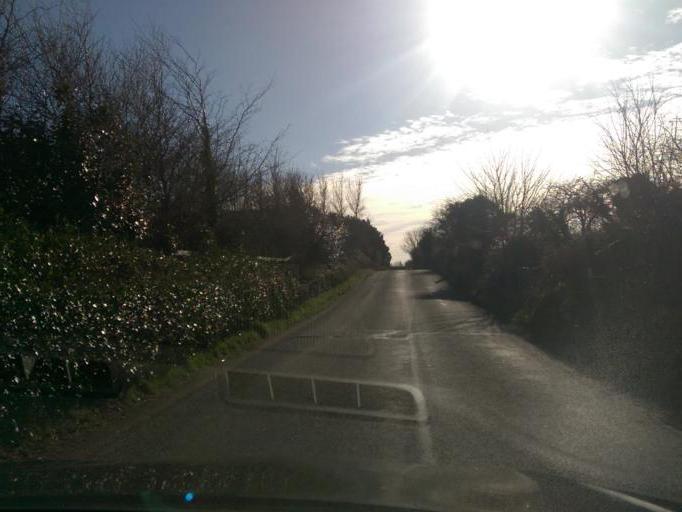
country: IE
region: Connaught
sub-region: County Galway
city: Oranmore
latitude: 53.2376
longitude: -8.9451
